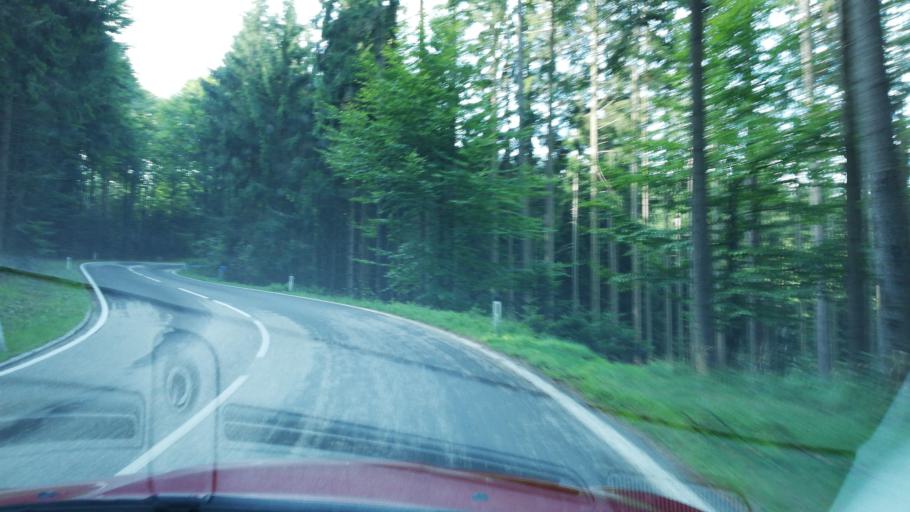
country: AT
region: Upper Austria
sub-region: Politischer Bezirk Vocklabruck
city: Redleiten
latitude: 48.1165
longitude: 13.5621
